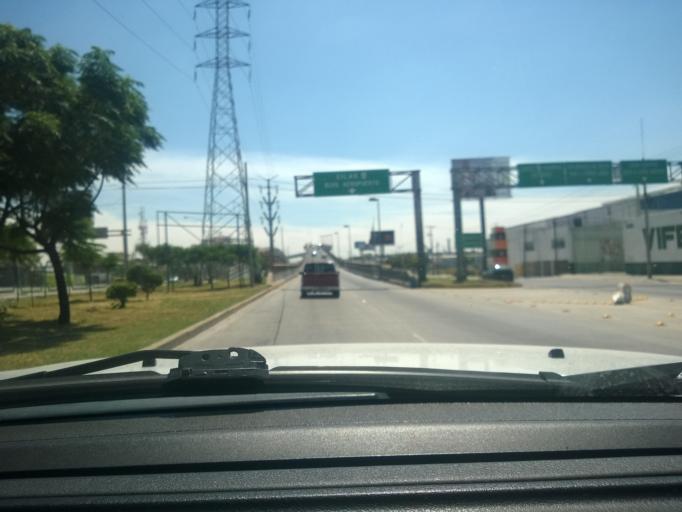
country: MX
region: Guanajuato
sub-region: Leon
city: Fraccionamiento Paraiso Real
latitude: 21.0985
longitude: -101.6253
